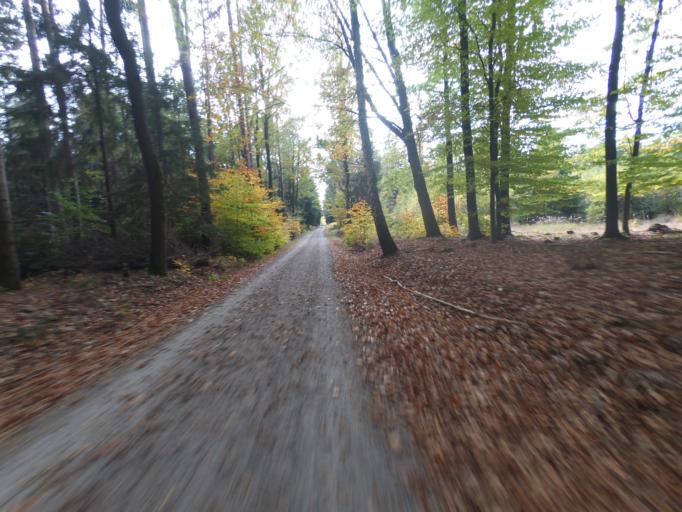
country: DE
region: Saxony
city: Radeberg
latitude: 51.0845
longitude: 13.8587
